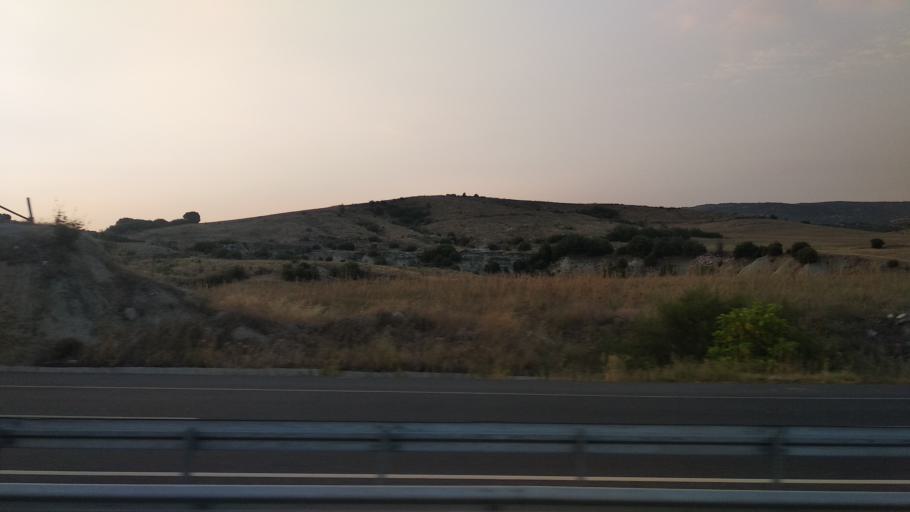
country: TR
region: Manisa
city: Selendi
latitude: 38.6253
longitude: 28.9300
